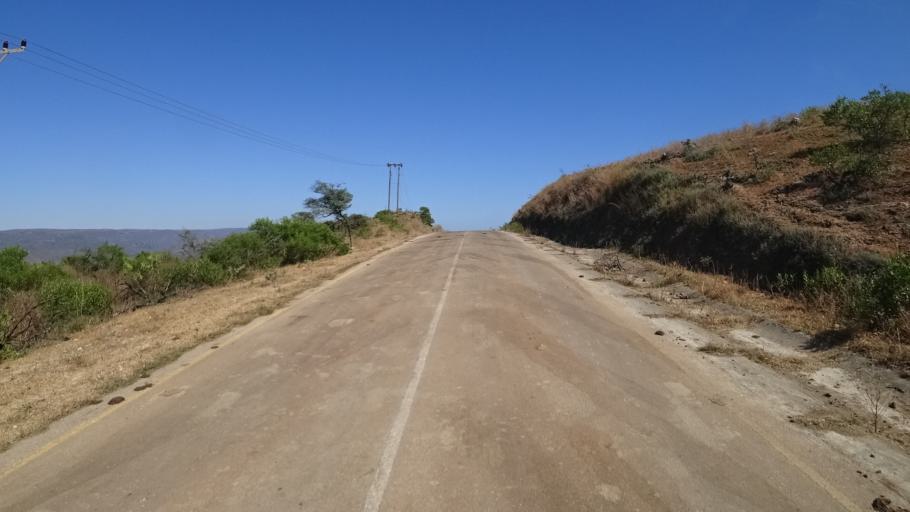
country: YE
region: Al Mahrah
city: Hawf
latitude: 16.7447
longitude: 53.3544
